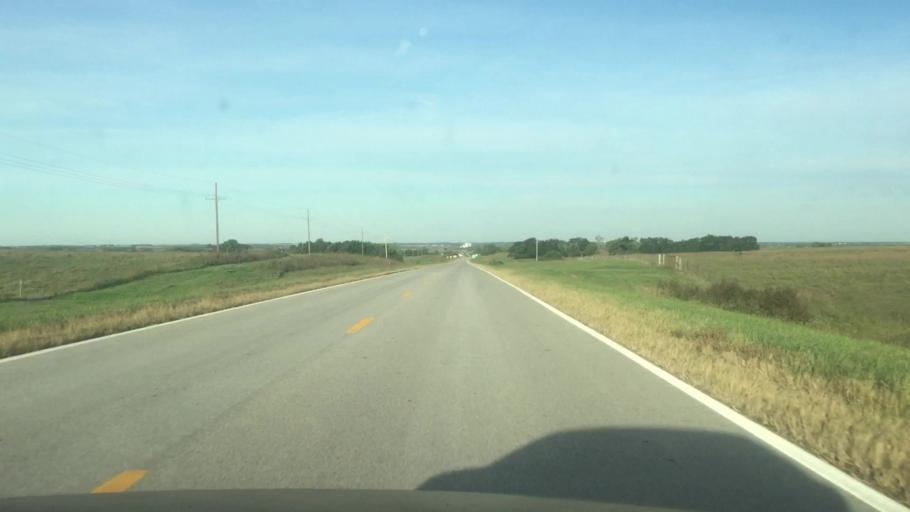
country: US
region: Nebraska
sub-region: Gage County
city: Wymore
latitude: 40.0451
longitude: -96.7349
